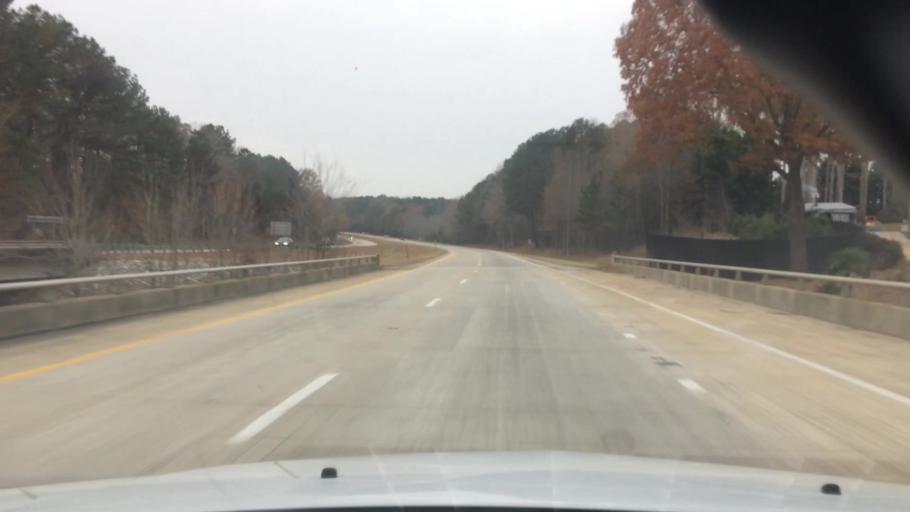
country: US
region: North Carolina
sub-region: Wake County
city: Zebulon
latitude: 35.8593
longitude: -78.2751
